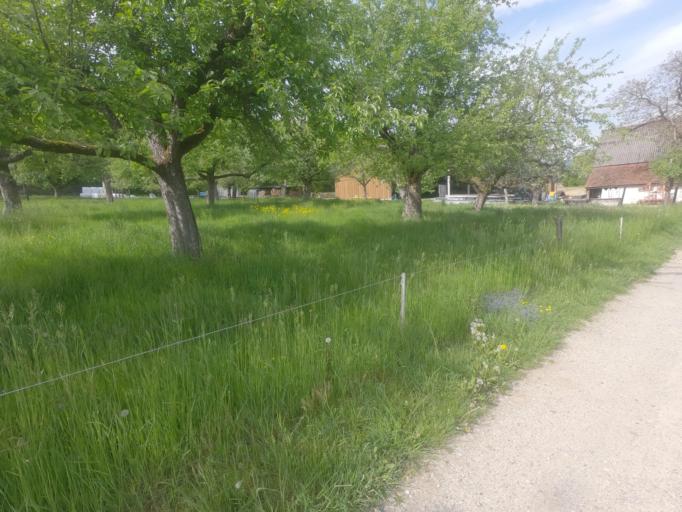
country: CH
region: Solothurn
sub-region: Bezirk Lebern
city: Riedholz
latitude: 47.2245
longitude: 7.5714
